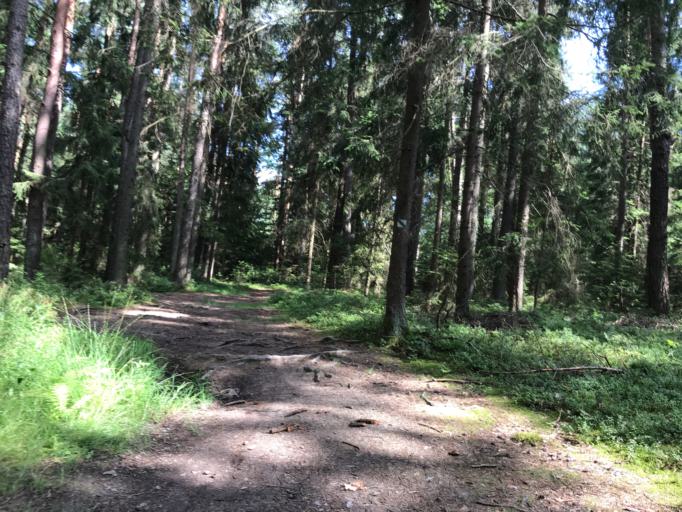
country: CZ
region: Jihocesky
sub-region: Okres Jindrichuv Hradec
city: Trebon
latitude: 48.9883
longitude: 14.7207
